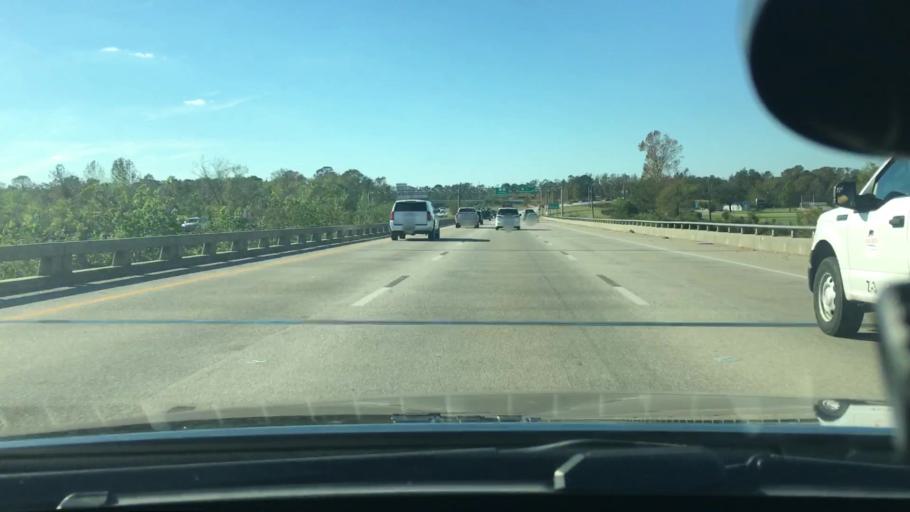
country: US
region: North Carolina
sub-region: Craven County
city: New Bern
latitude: 35.0988
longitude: -77.0517
